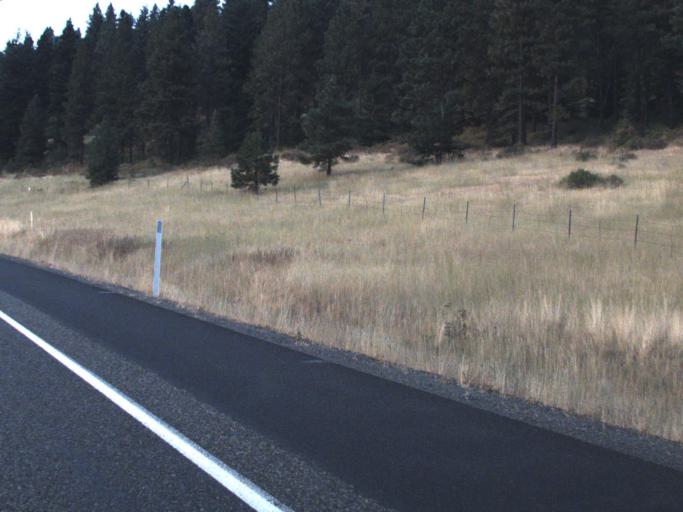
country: US
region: Washington
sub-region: Kittitas County
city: Cle Elum
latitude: 47.1853
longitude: -120.7069
